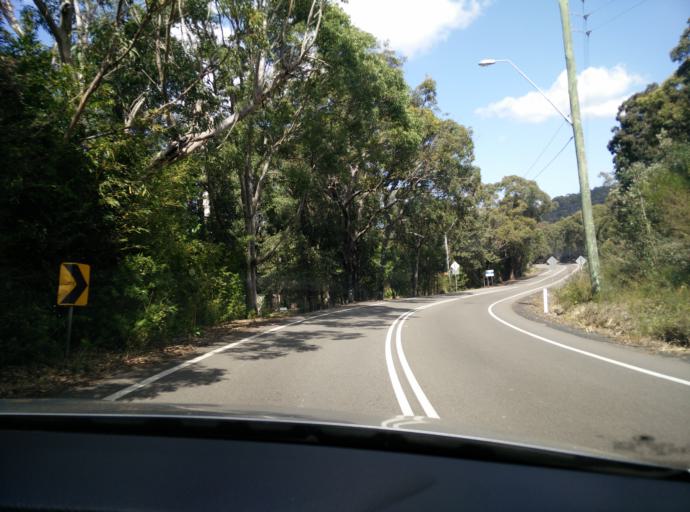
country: AU
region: New South Wales
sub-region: Gosford Shire
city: Blackwall
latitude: -33.4856
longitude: 151.3055
